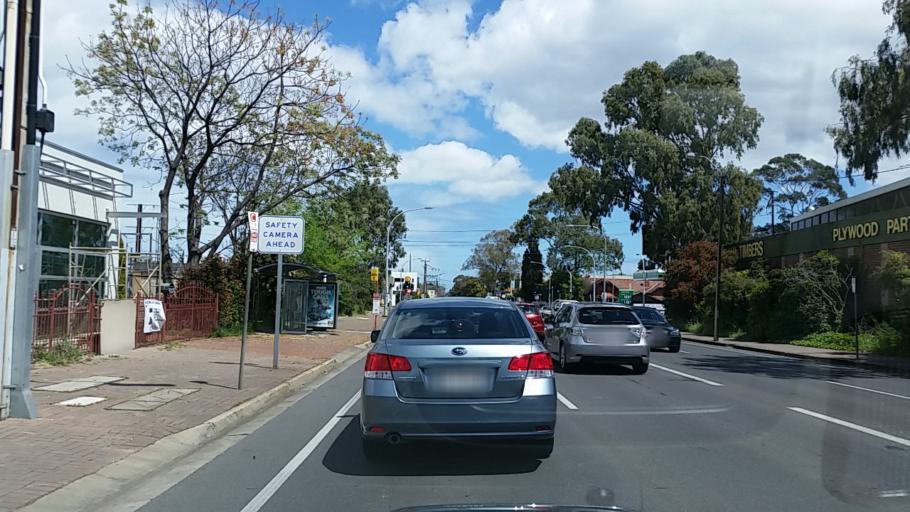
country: AU
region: South Australia
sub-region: Norwood Payneham St Peters
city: Trinity Gardens
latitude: -34.9148
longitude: 138.6418
